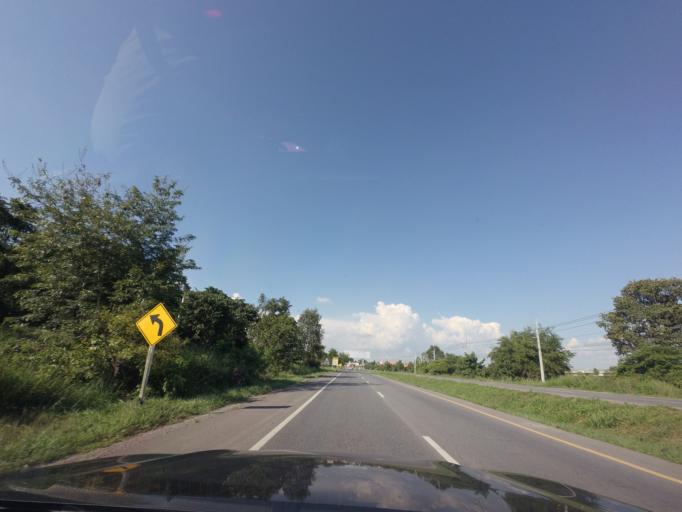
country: TH
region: Khon Kaen
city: Non Sila
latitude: 15.9581
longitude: 102.6877
